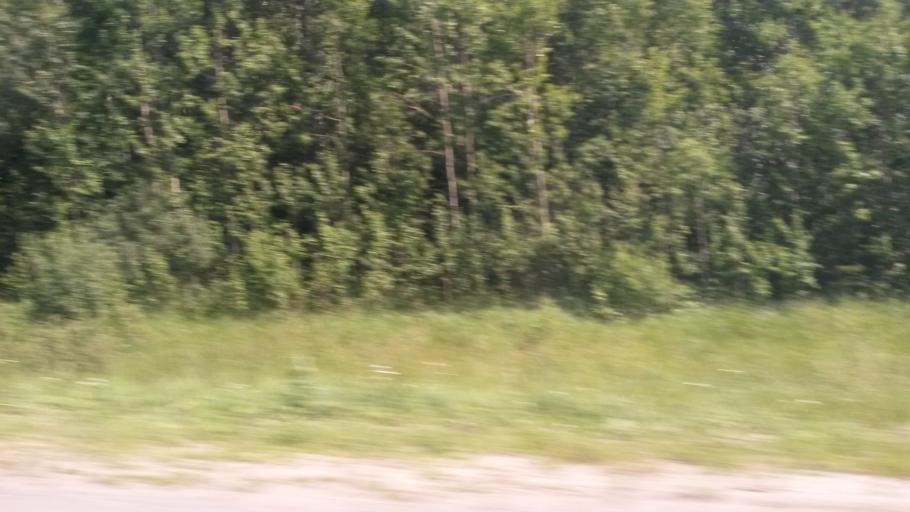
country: RU
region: Ivanovo
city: Rodniki
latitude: 57.1096
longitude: 41.7809
